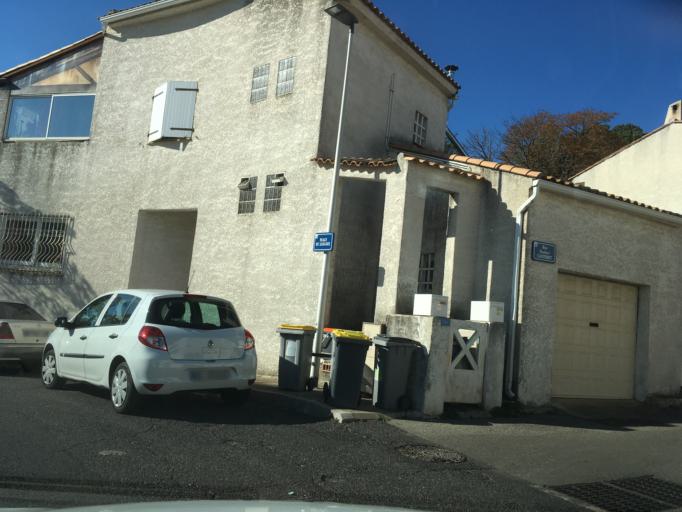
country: FR
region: Languedoc-Roussillon
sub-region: Departement de l'Herault
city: Saint-Jean-de-Vedas
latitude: 43.5984
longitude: 3.8334
